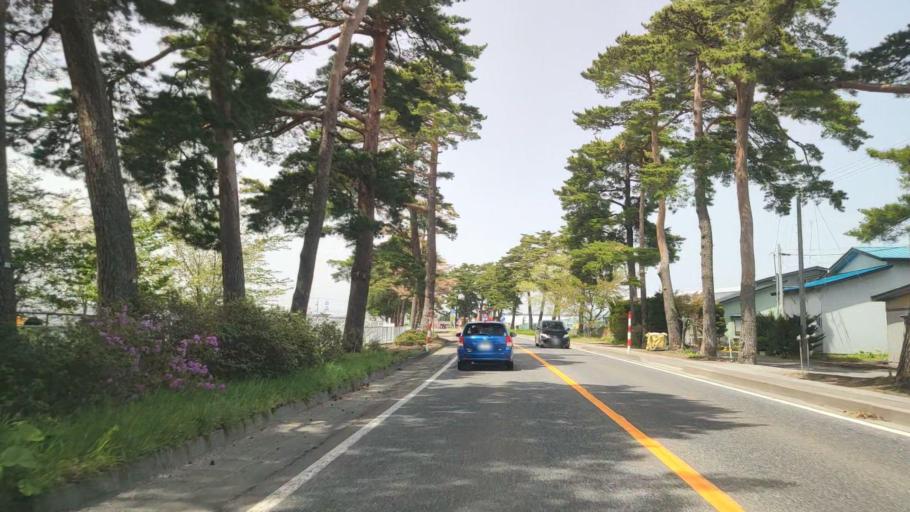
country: JP
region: Aomori
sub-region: Misawa Shi
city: Inuotose
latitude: 40.6709
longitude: 141.1834
